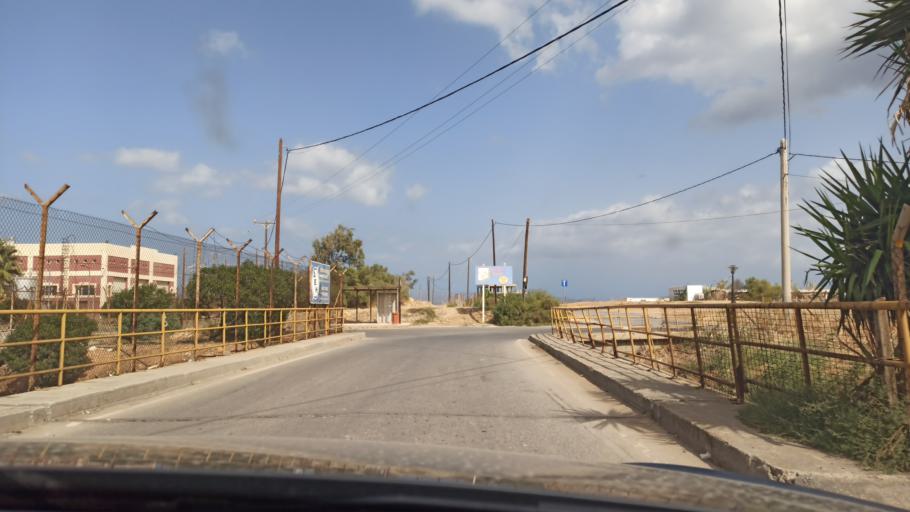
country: GR
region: Crete
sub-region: Nomos Irakleiou
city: Gazi
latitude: 35.3399
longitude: 25.0531
